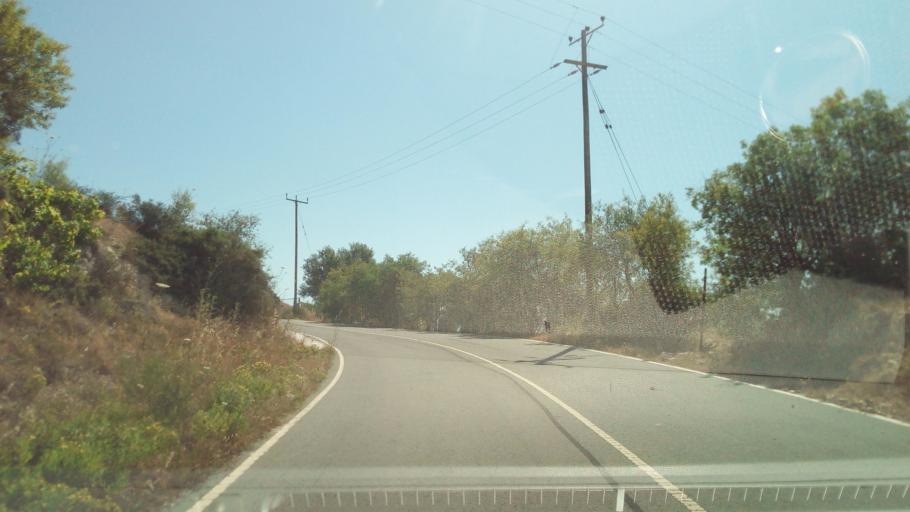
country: CY
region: Limassol
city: Pachna
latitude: 34.8035
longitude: 32.6801
